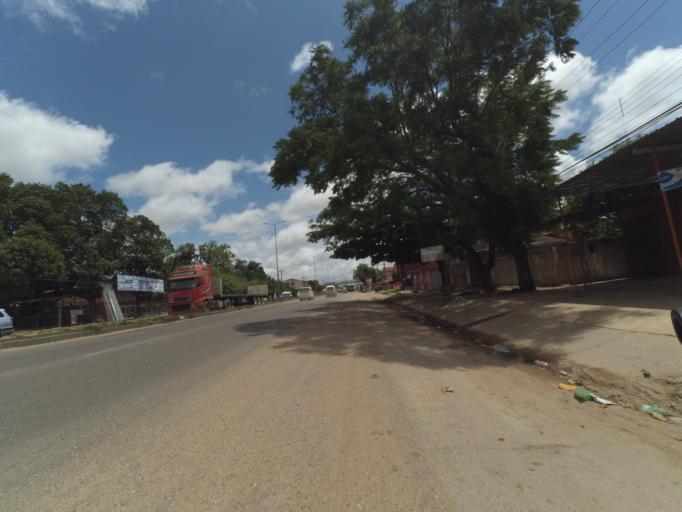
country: BO
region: Santa Cruz
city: Santa Cruz de la Sierra
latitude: -17.8507
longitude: -63.2520
